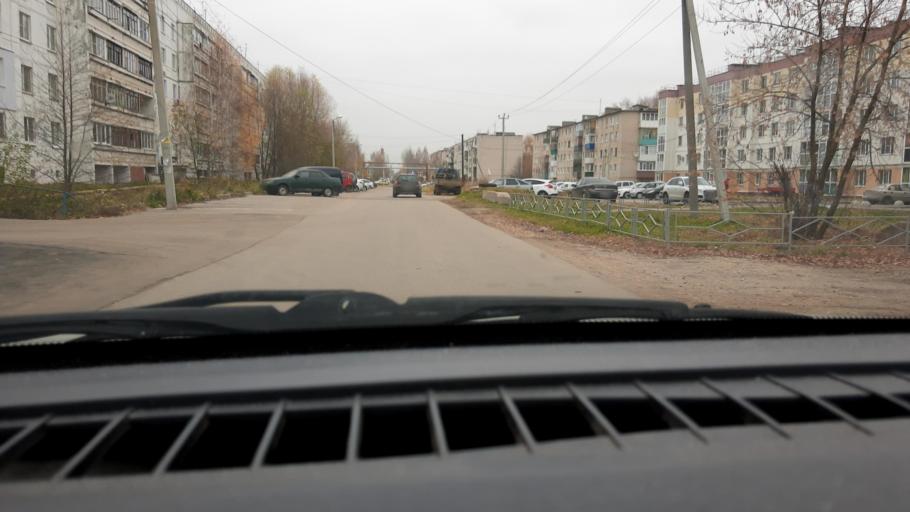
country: RU
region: Nizjnij Novgorod
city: Afonino
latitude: 56.2083
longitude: 44.0976
